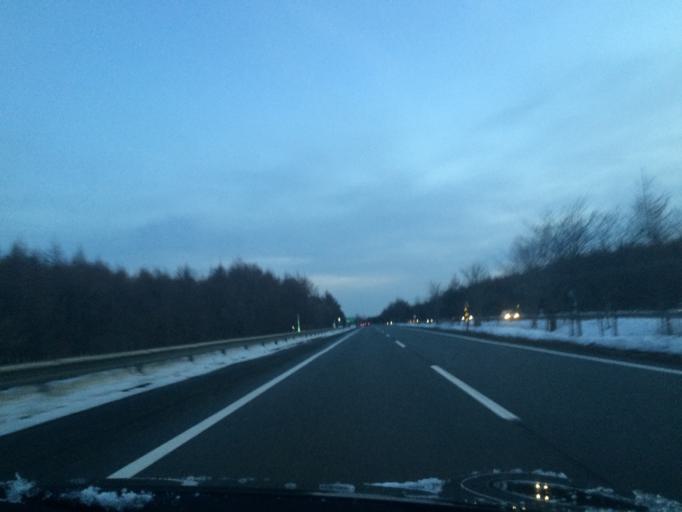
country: JP
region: Hokkaido
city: Chitose
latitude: 42.7903
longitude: 141.6268
